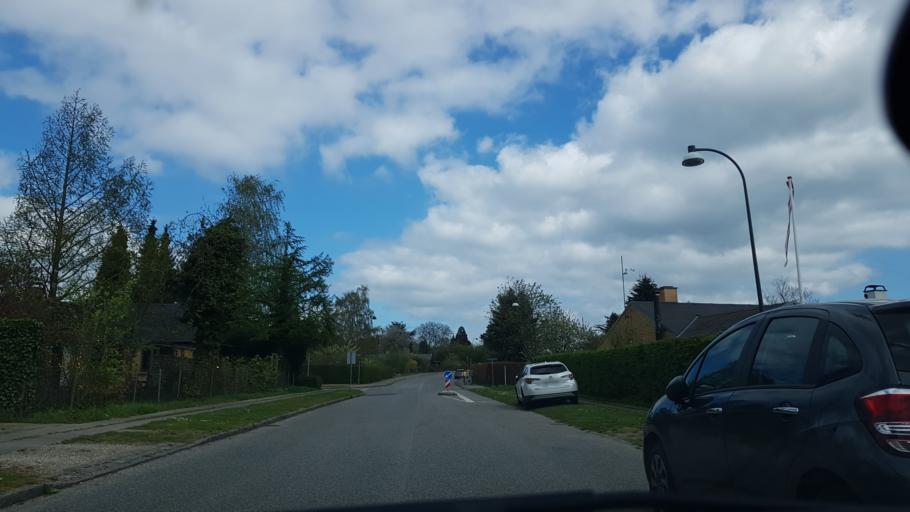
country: DK
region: Capital Region
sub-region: Rudersdal Kommune
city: Trorod
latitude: 55.8408
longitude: 12.5412
